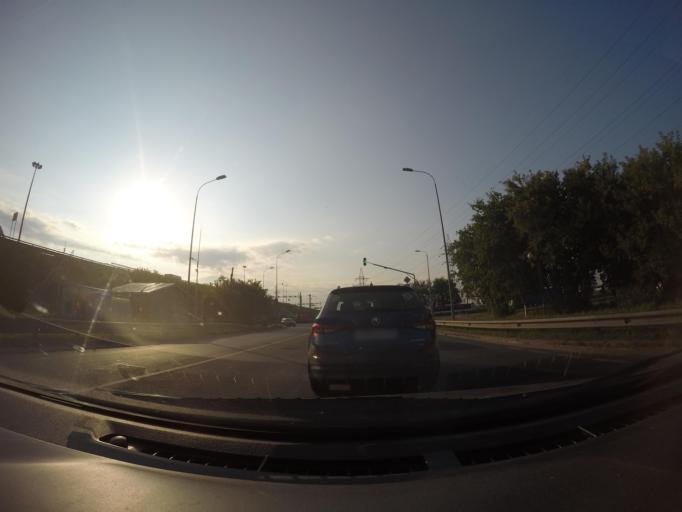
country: RU
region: Moskovskaya
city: Lyubertsy
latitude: 55.6651
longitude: 37.8786
